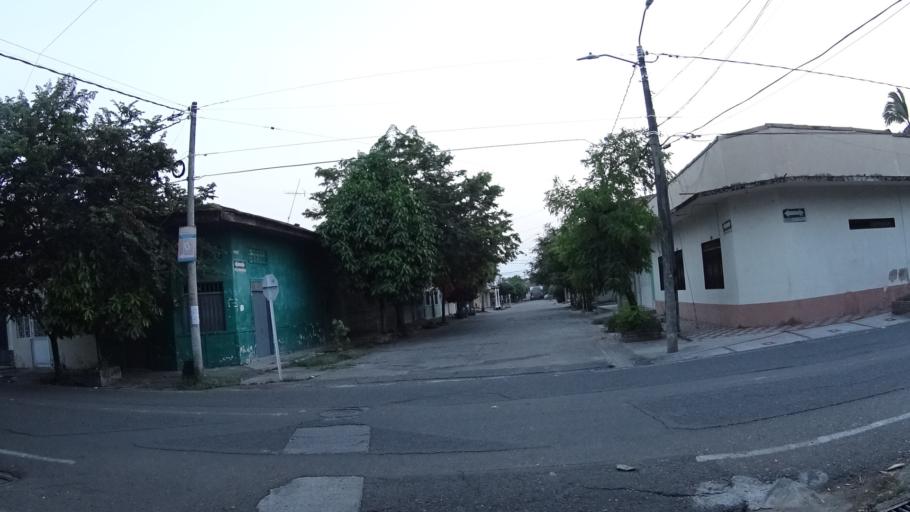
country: CO
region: Caldas
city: La Dorada
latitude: 5.4483
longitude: -74.6627
